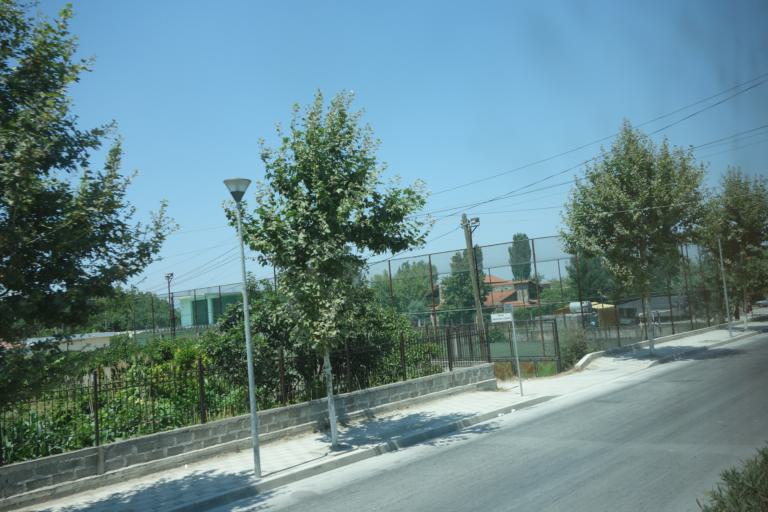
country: AL
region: Fier
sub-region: Rrethi i Fierit
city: Mbrostar-Ure
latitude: 40.7404
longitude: 19.5757
